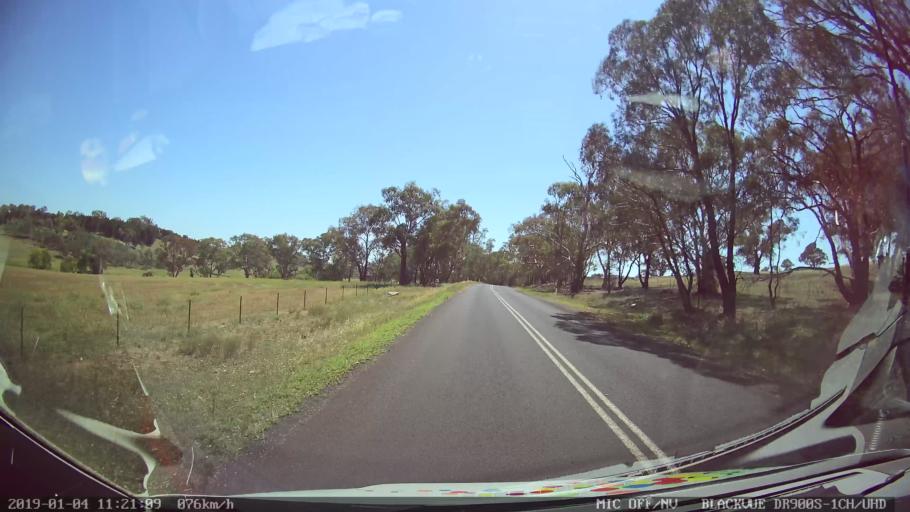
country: AU
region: New South Wales
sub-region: Cabonne
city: Molong
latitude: -33.1565
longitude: 148.7078
